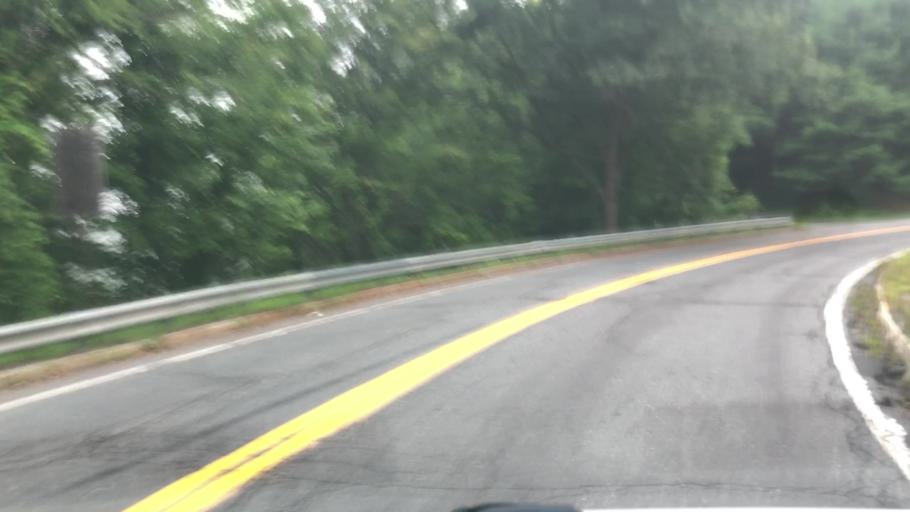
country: US
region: Massachusetts
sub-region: Franklin County
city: Shelburne Falls
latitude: 42.6181
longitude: -72.7452
